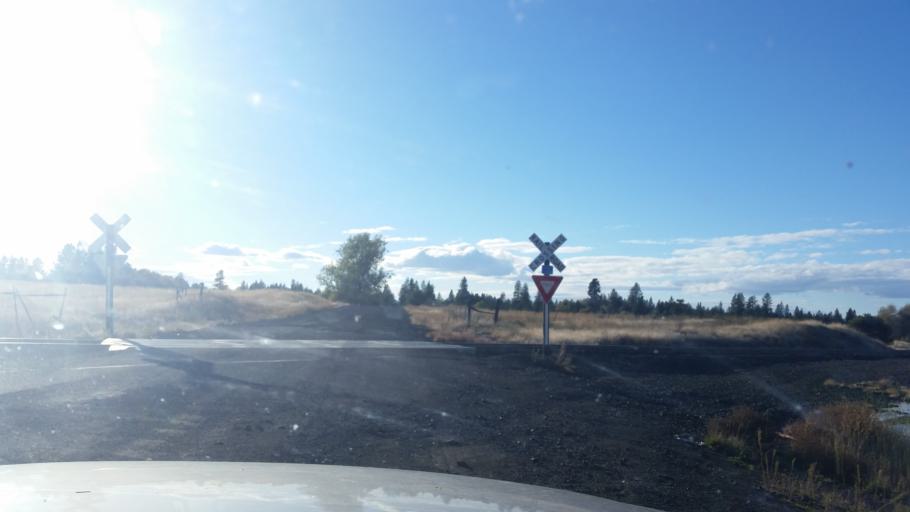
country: US
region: Washington
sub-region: Spokane County
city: Fairchild Air Force Base
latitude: 47.5801
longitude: -117.6204
